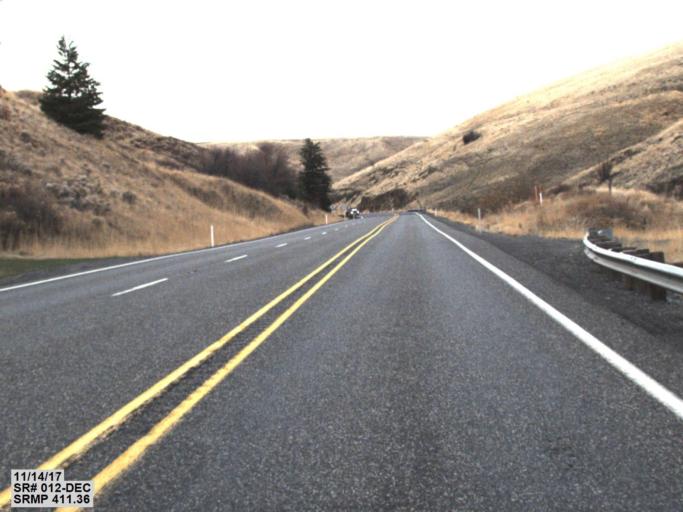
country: US
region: Washington
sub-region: Garfield County
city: Pomeroy
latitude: 46.4458
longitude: -117.4571
